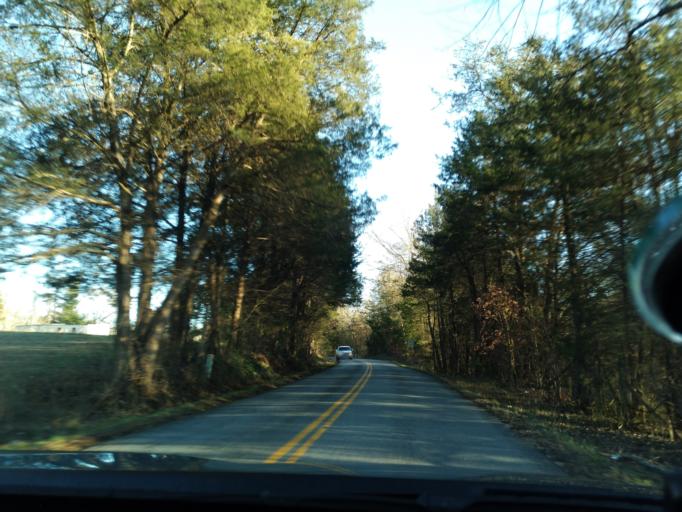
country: US
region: Virginia
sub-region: Prince Edward County
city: Hampden Sydney
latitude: 37.3083
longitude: -78.5633
